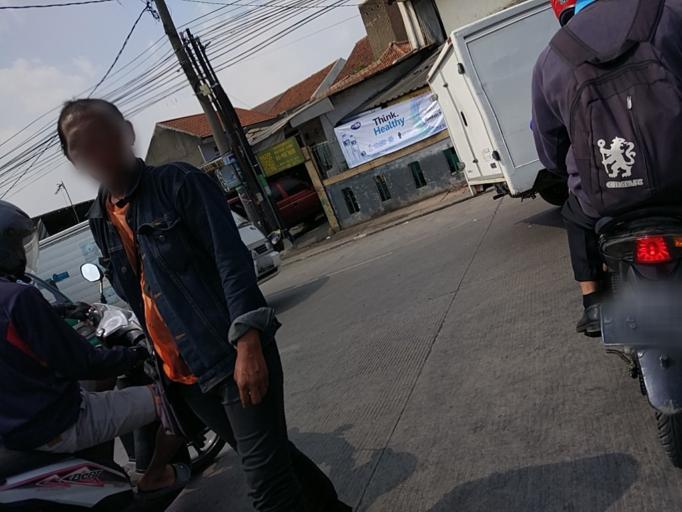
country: ID
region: West Java
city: Bandung
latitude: -6.9229
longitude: 107.5749
